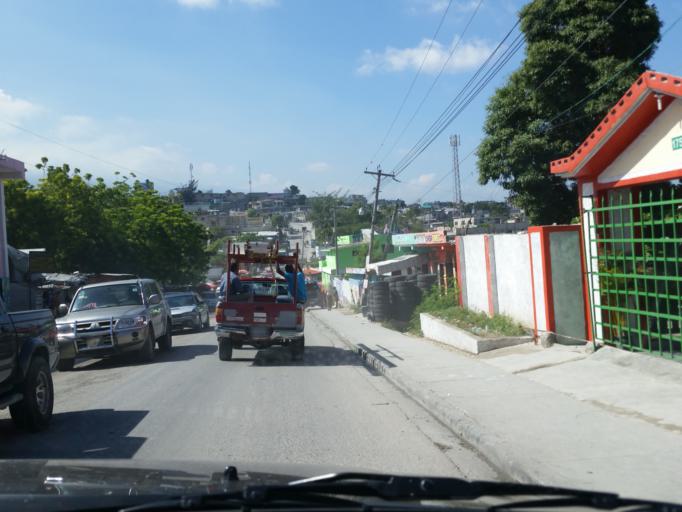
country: HT
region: Ouest
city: Delmas 73
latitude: 18.5645
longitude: -72.2894
